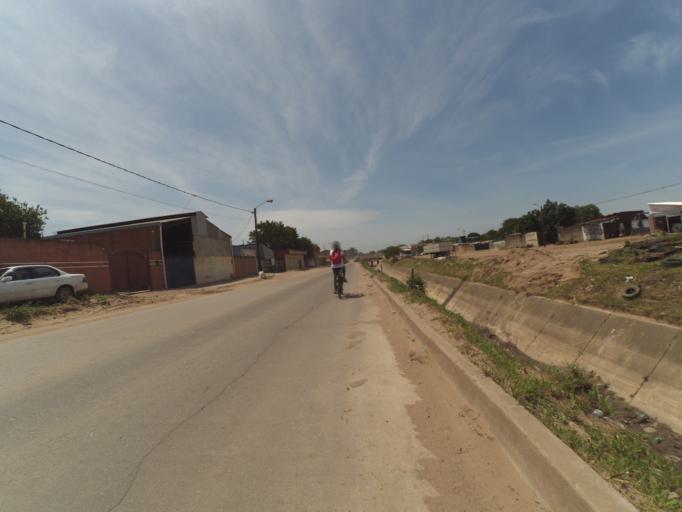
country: BO
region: Santa Cruz
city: Santa Cruz de la Sierra
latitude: -17.8329
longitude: -63.2409
